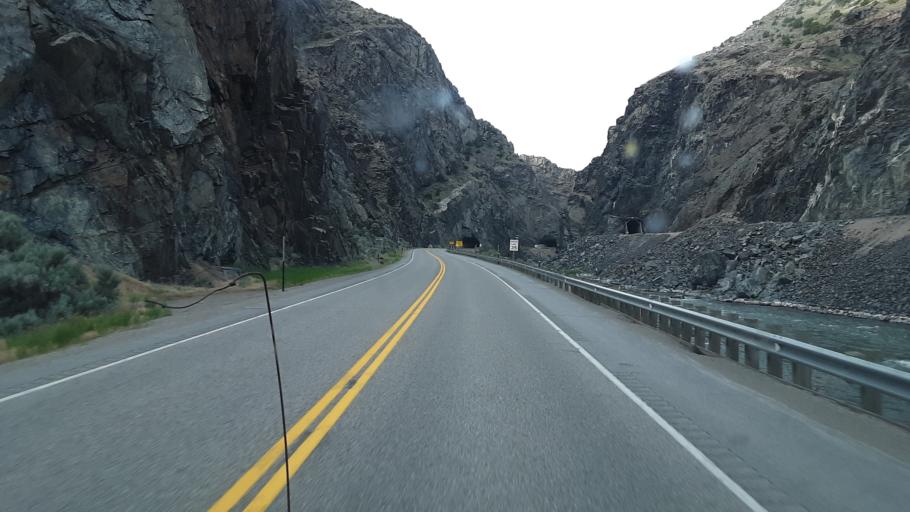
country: US
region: Wyoming
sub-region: Hot Springs County
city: Thermopolis
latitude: 43.4511
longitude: -108.1696
